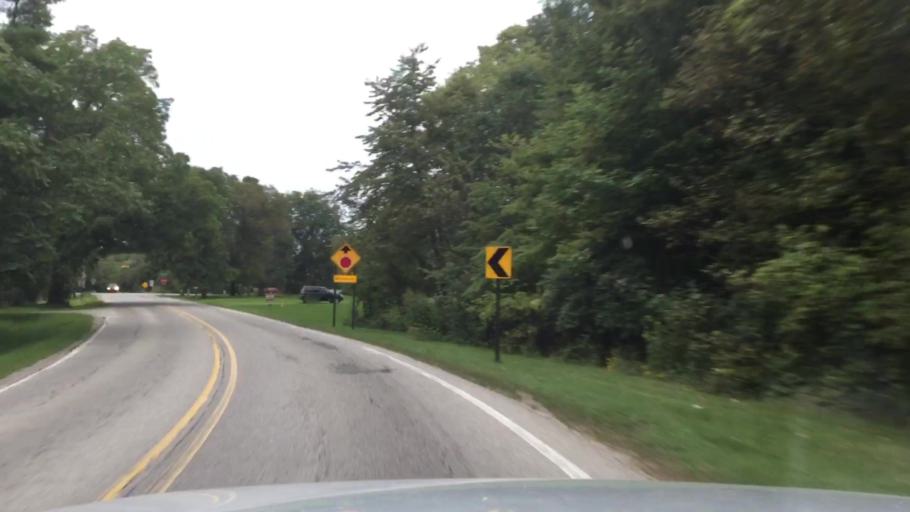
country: US
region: Michigan
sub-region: Washtenaw County
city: Milan
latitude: 42.1047
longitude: -83.7336
